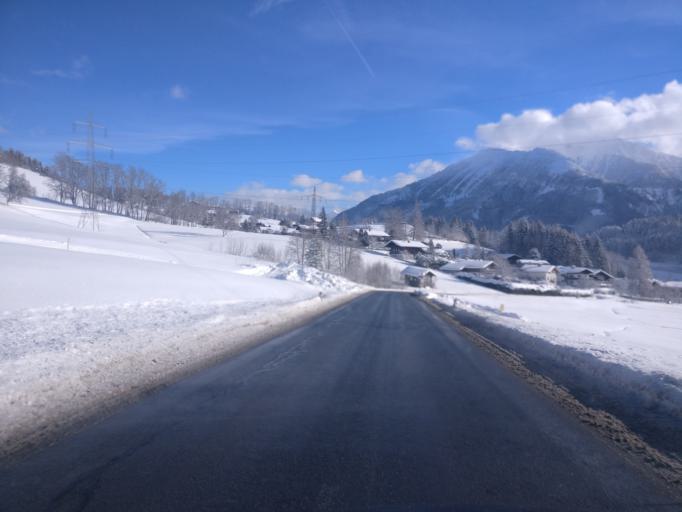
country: AT
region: Salzburg
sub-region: Politischer Bezirk Sankt Johann im Pongau
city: Goldegg
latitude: 47.3230
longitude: 13.0982
